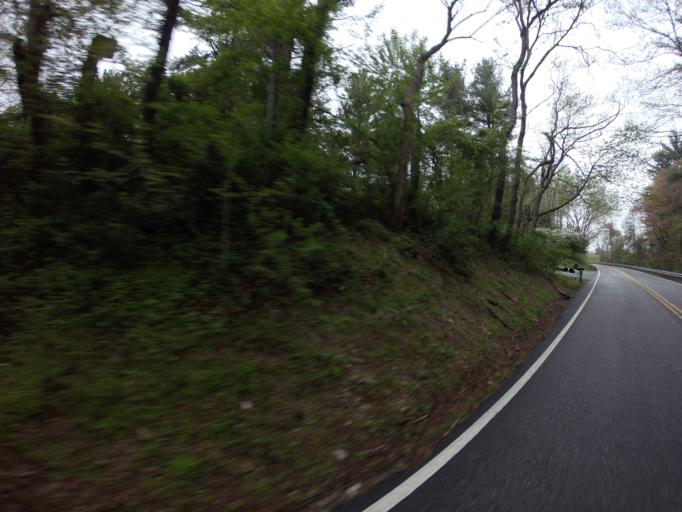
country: US
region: Maryland
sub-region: Carroll County
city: Hampstead
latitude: 39.5719
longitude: -76.7533
